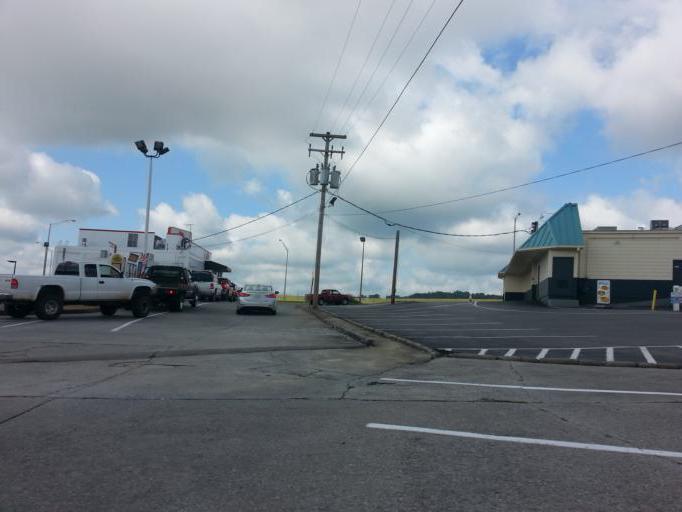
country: US
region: Tennessee
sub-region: Blount County
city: Alcoa
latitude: 35.8185
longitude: -83.9789
